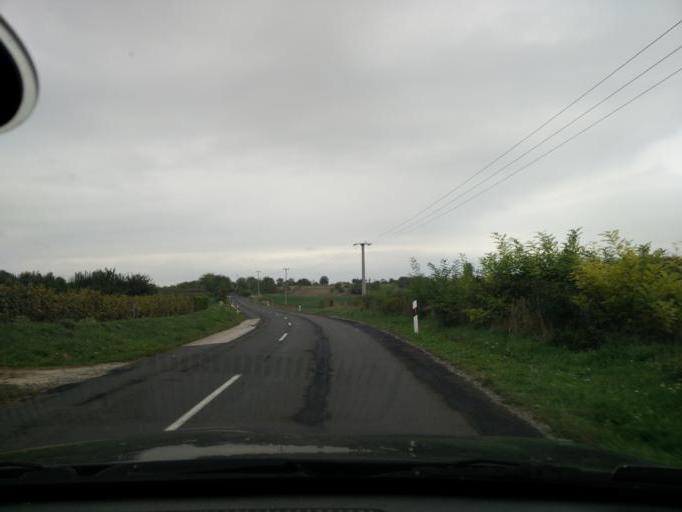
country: HU
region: Komarom-Esztergom
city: Tat
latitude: 47.7217
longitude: 18.6332
